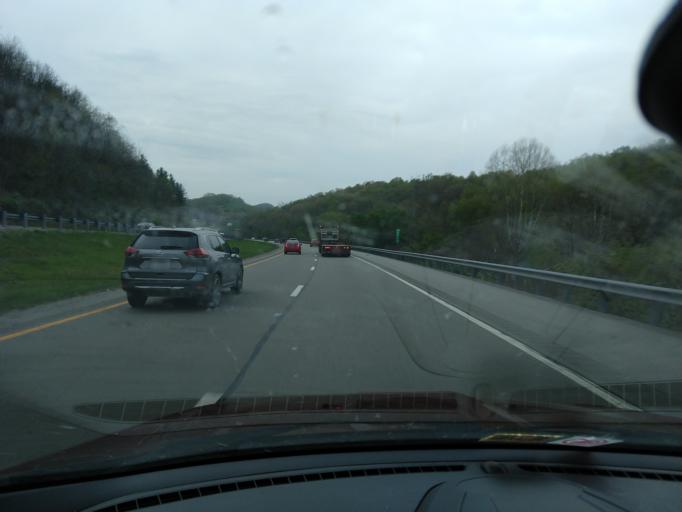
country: US
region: West Virginia
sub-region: Harrison County
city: Stonewood
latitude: 39.1516
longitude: -80.3583
